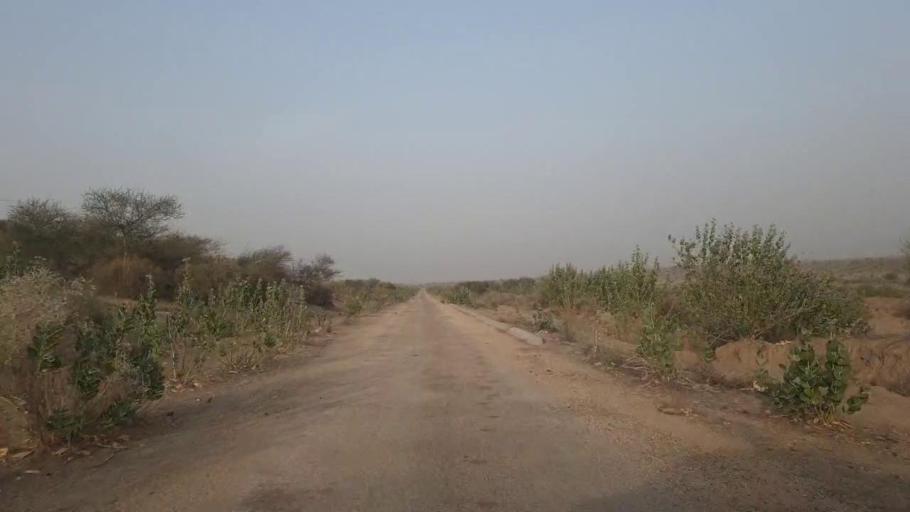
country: PK
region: Sindh
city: Chor
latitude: 25.4963
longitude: 69.9256
